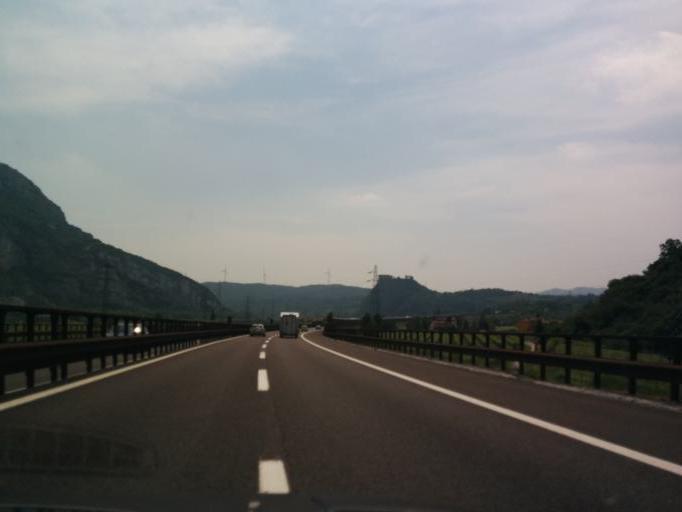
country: IT
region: Veneto
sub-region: Provincia di Verona
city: Dolce
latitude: 45.5887
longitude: 10.8351
